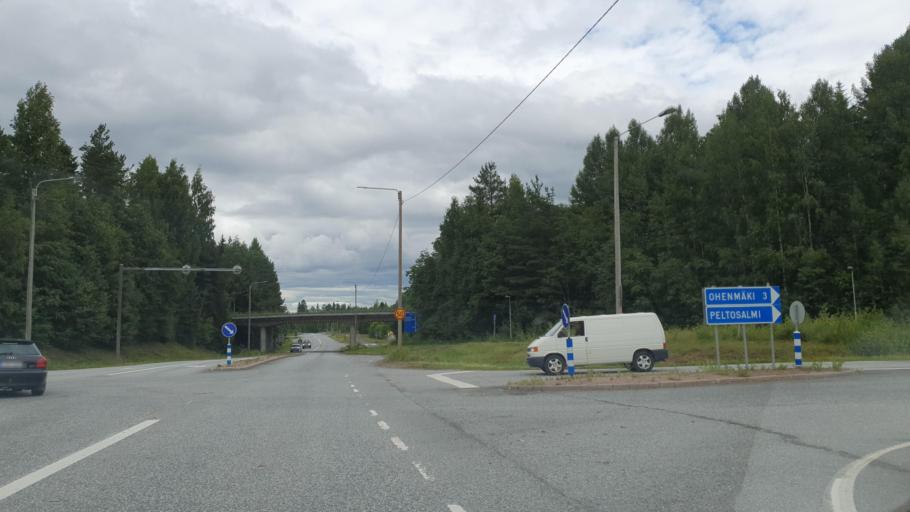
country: FI
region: Northern Savo
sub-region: Ylae-Savo
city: Iisalmi
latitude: 63.5222
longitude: 27.2428
